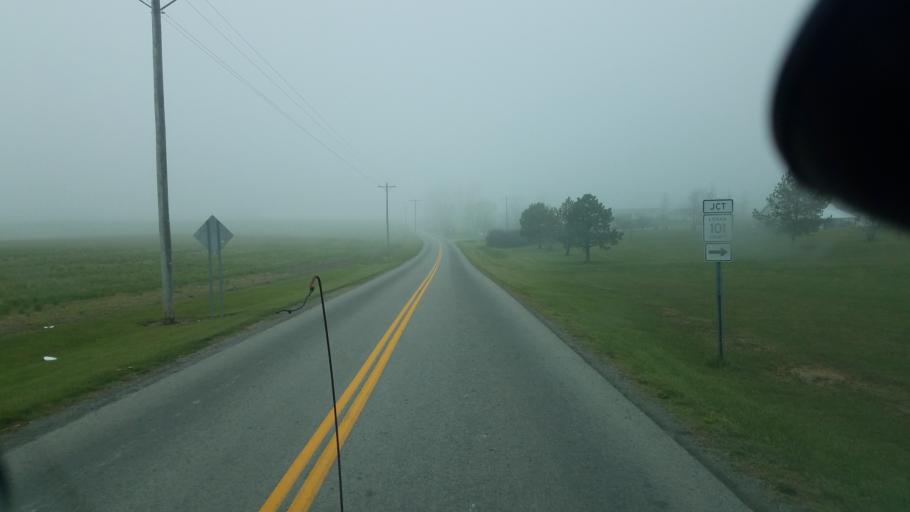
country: US
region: Ohio
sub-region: Logan County
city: Northwood
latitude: 40.4534
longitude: -83.7593
